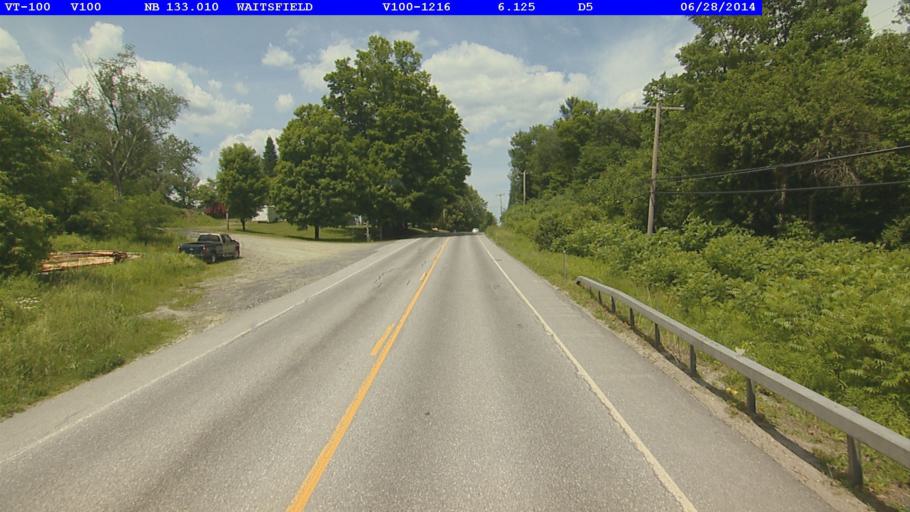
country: US
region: Vermont
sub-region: Washington County
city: Waterbury
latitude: 44.2163
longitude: -72.7921
